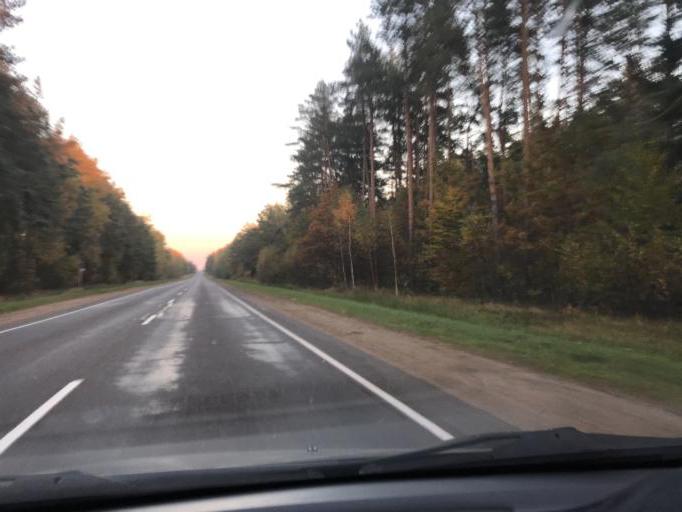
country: BY
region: Mogilev
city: Hlusha
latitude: 53.0943
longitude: 28.9579
